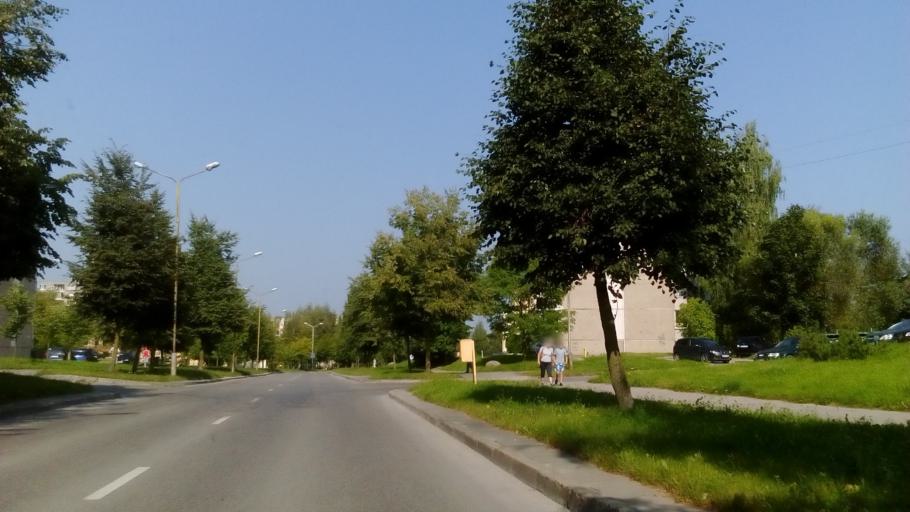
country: LT
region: Alytaus apskritis
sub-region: Alytus
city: Alytus
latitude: 54.3967
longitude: 24.0200
